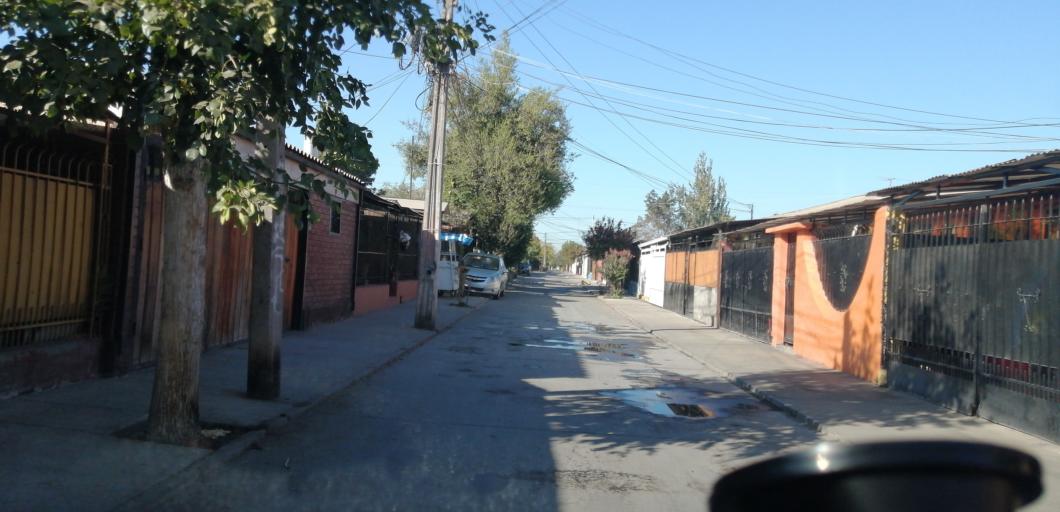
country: CL
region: Santiago Metropolitan
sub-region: Provincia de Santiago
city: Lo Prado
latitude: -33.4310
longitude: -70.7512
